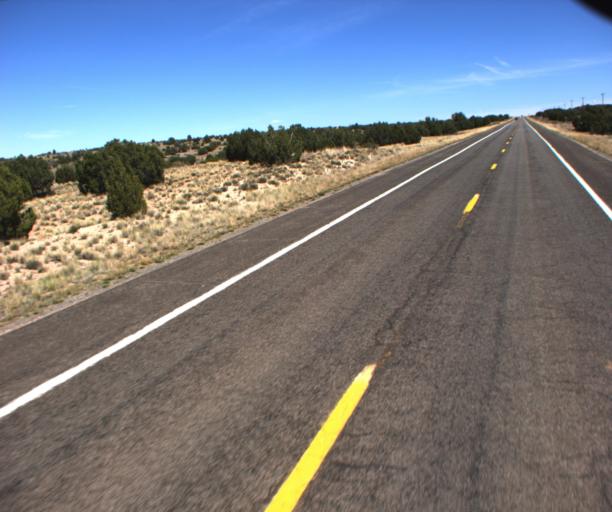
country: US
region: Arizona
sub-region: Mohave County
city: Peach Springs
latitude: 35.4968
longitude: -113.5385
